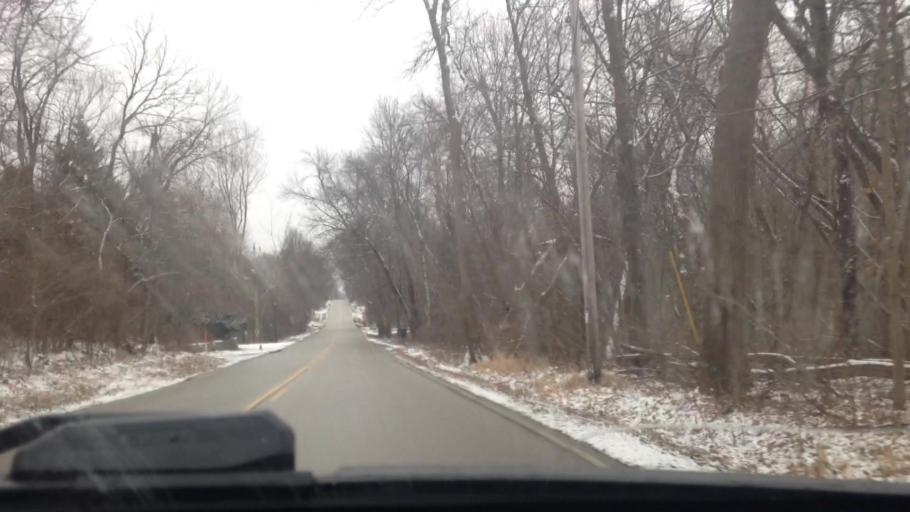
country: US
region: Wisconsin
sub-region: Waukesha County
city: Lannon
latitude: 43.1804
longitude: -88.1827
